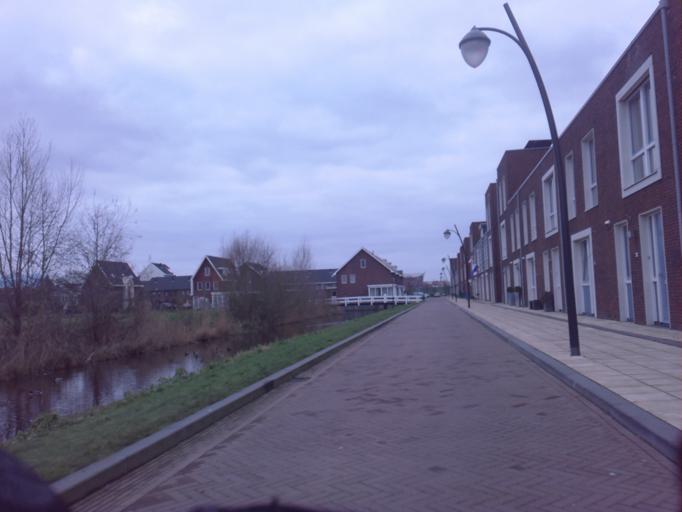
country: NL
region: Utrecht
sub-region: Gemeente Amersfoort
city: Randenbroek
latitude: 52.1856
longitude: 5.4238
